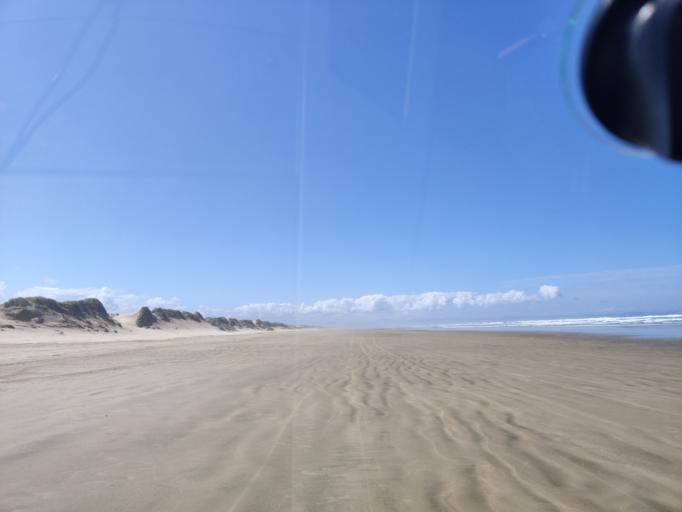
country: NZ
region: Northland
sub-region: Far North District
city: Kaitaia
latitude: -34.9208
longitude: 173.1008
